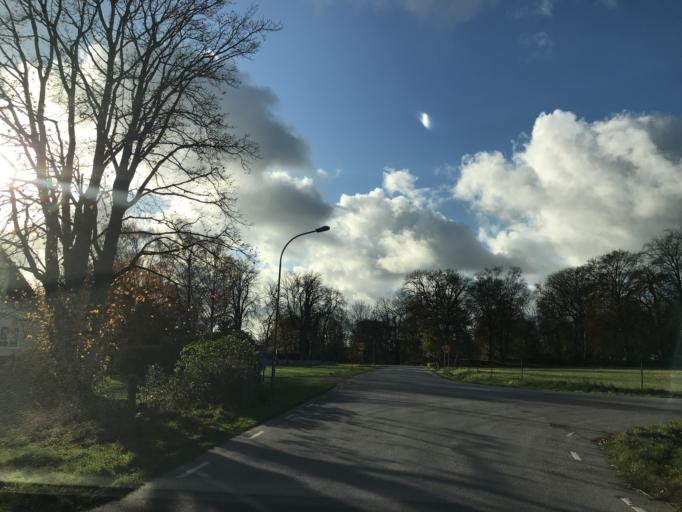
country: SE
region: Skane
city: Smygehamn
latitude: 55.3836
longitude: 13.4243
